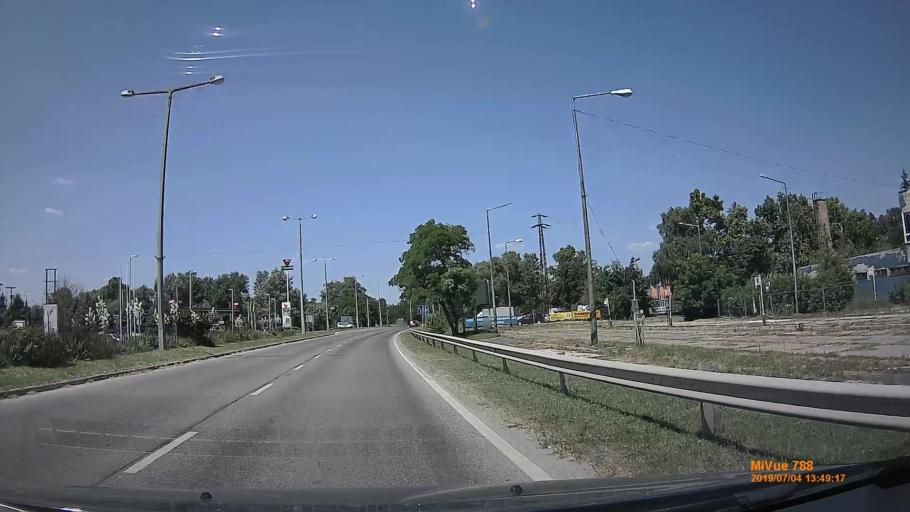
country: HU
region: Komarom-Esztergom
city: Tatabanya
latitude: 47.5955
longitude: 18.3881
